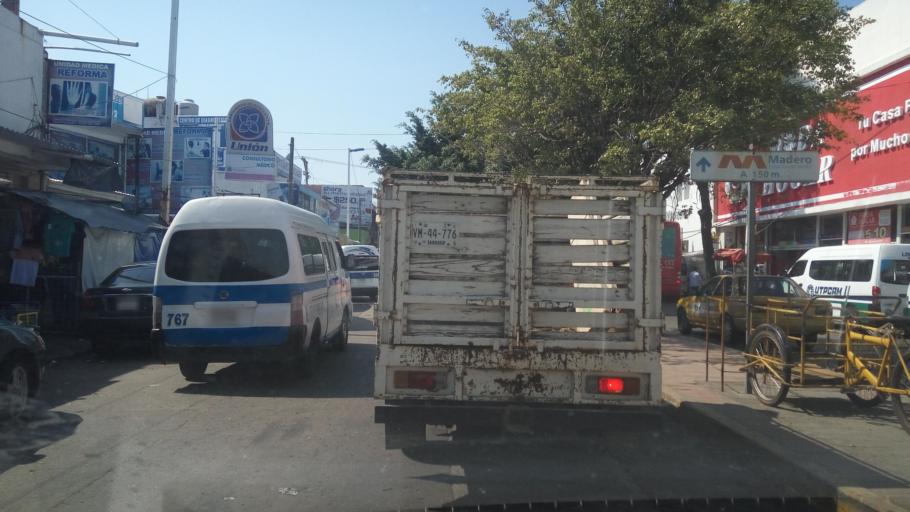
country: MX
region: Tabasco
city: Villahermosa
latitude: 17.9972
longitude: -92.9156
